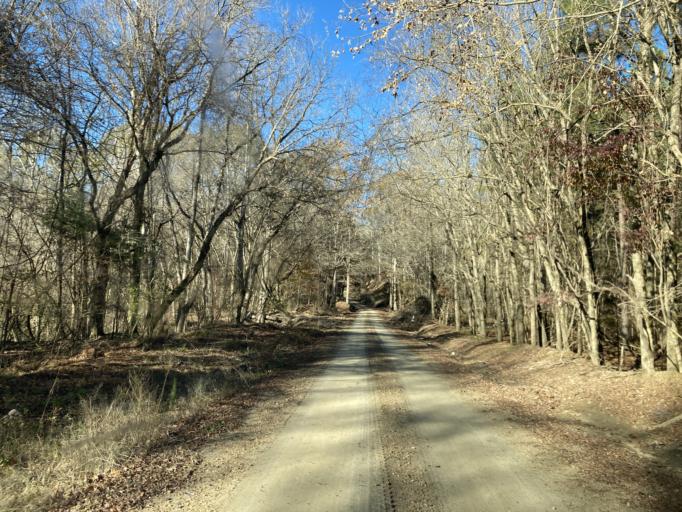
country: US
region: Mississippi
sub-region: Yazoo County
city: Yazoo City
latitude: 32.7069
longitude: -90.4722
